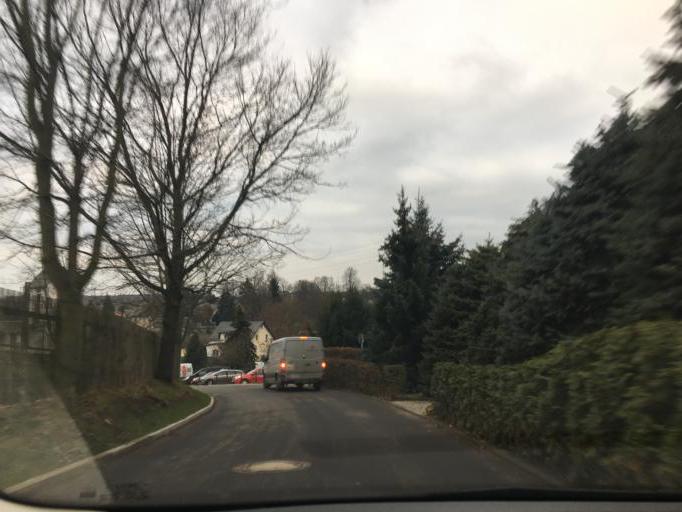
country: DE
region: Saxony
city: Niederfrohna
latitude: 50.8734
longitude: 12.7068
